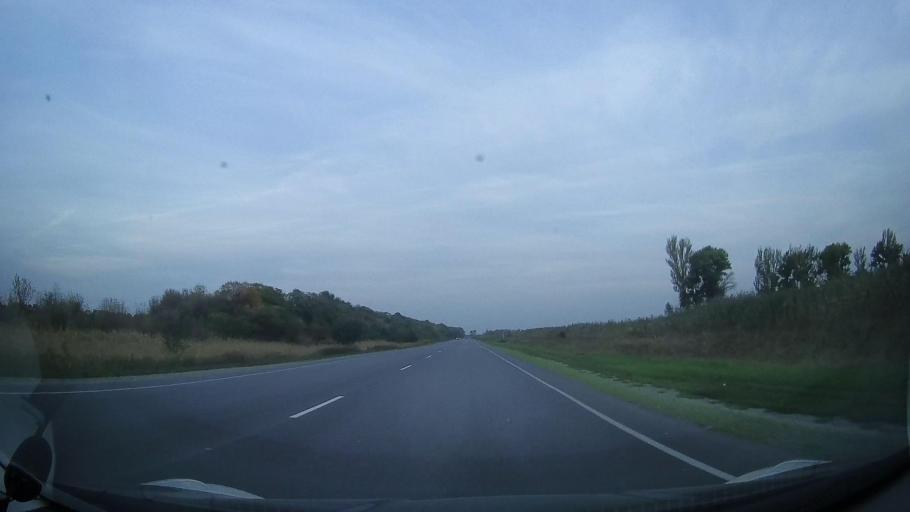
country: RU
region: Rostov
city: Ol'ginskaya
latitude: 47.1309
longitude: 39.9389
